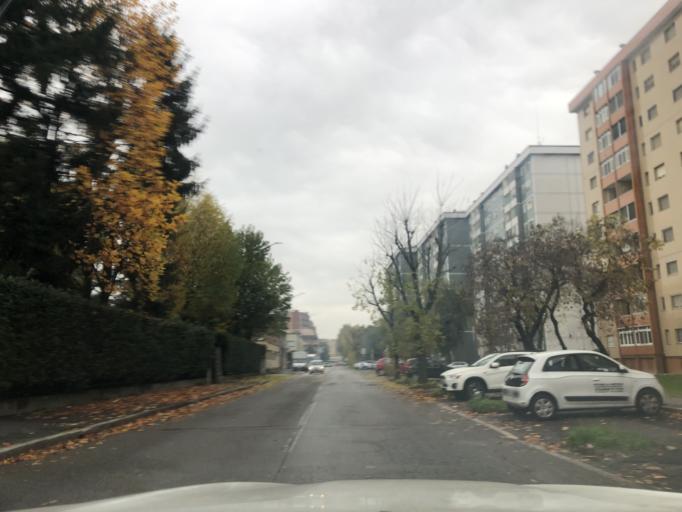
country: IT
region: Lombardy
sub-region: Citta metropolitana di Milano
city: Cesano Boscone
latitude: 45.4358
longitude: 9.0932
